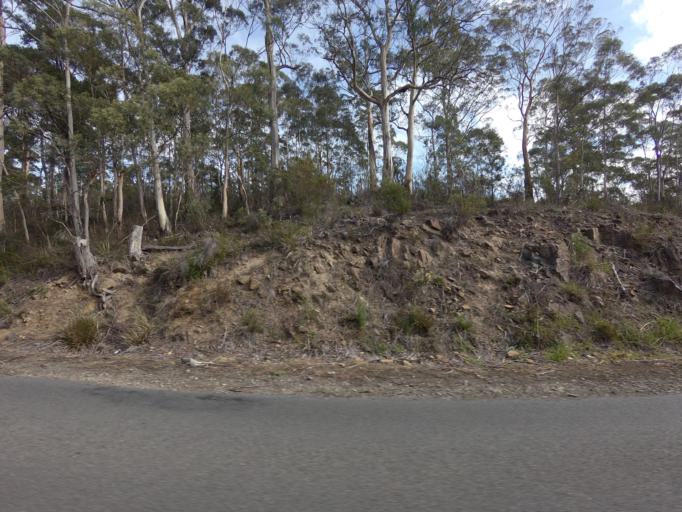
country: AU
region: Tasmania
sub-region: Clarence
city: Sandford
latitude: -43.1220
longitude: 147.7650
